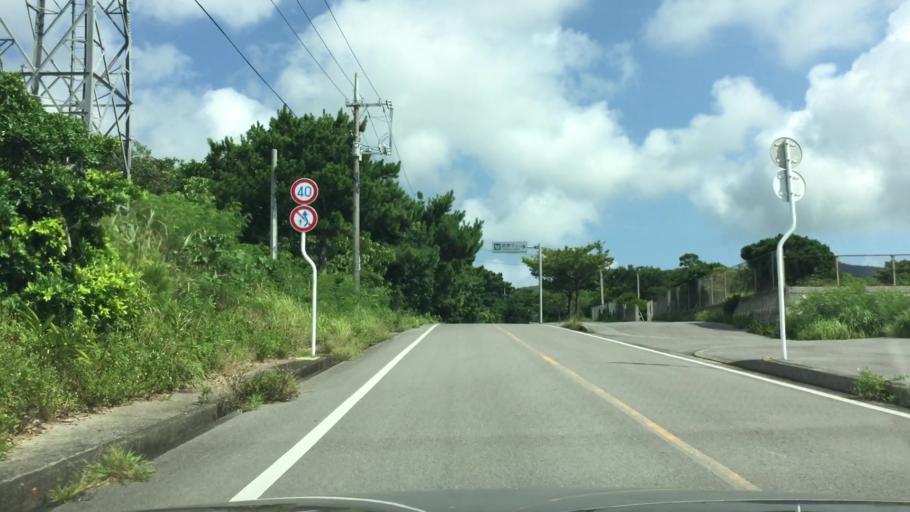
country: JP
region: Okinawa
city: Ishigaki
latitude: 24.4201
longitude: 124.2144
